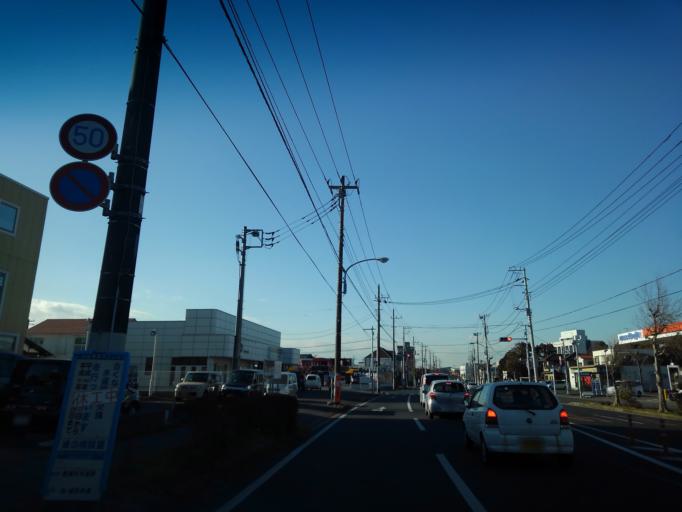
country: JP
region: Chiba
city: Kimitsu
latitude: 35.3268
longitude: 139.9063
